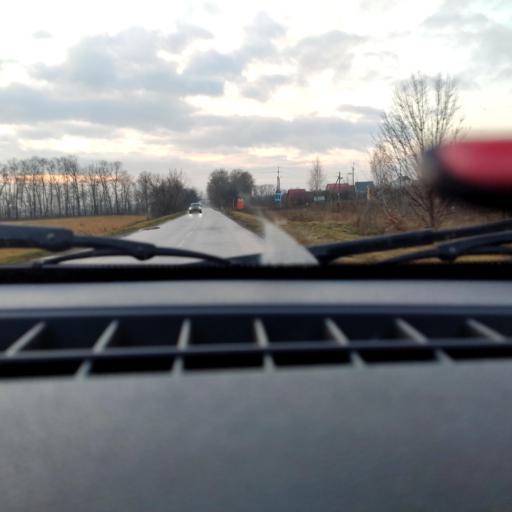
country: RU
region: Bashkortostan
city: Avdon
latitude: 54.5093
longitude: 55.8343
